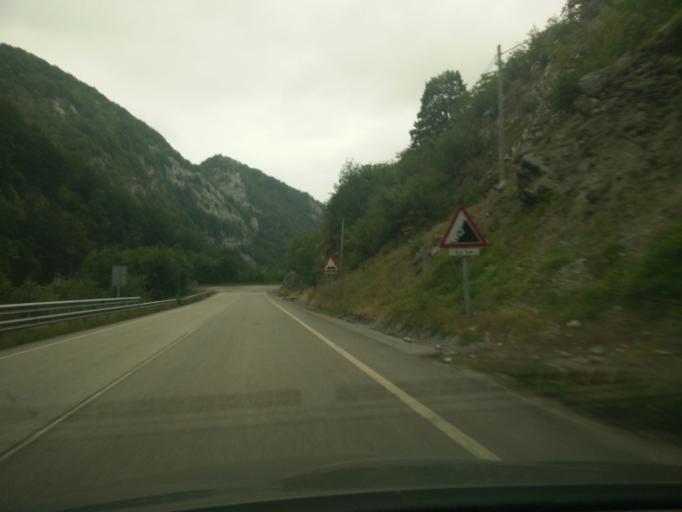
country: ES
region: Asturias
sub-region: Province of Asturias
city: Campo de Caso
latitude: 43.1798
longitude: -5.3614
